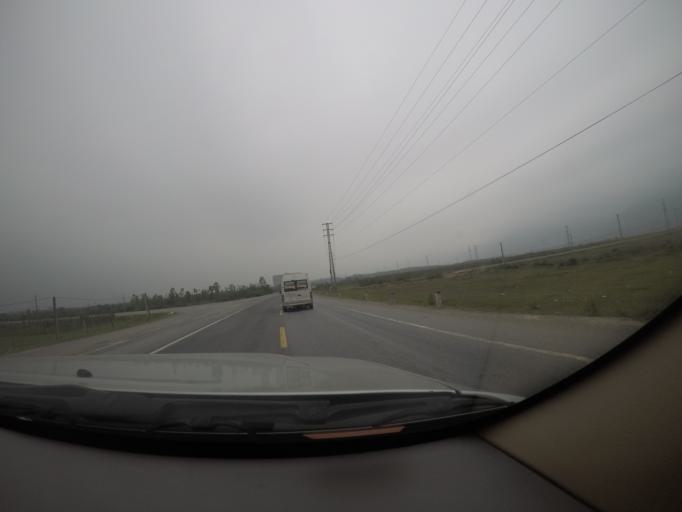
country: VN
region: Ha Tinh
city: Ky Anh
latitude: 18.0204
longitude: 106.3825
